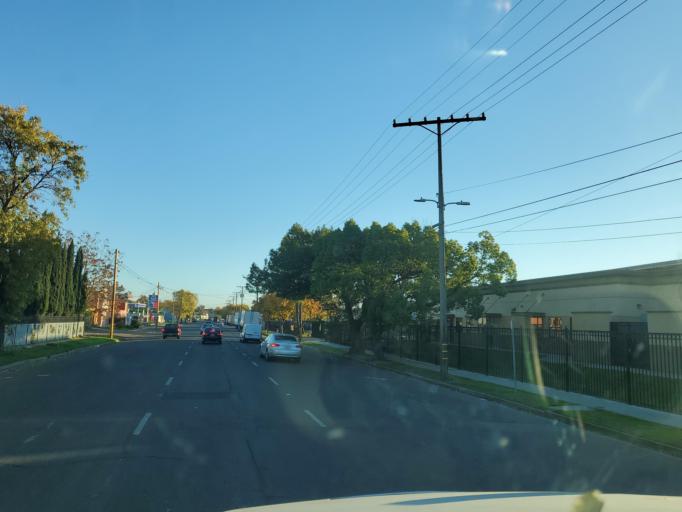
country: US
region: California
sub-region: San Joaquin County
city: Stockton
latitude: 37.9372
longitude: -121.2865
